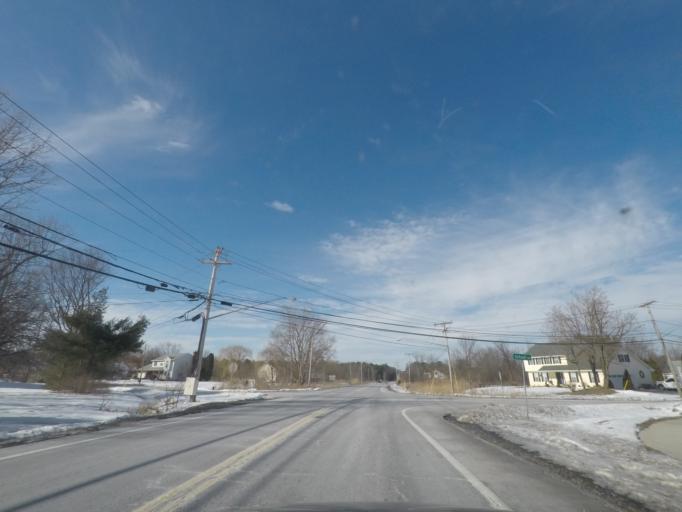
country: US
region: New York
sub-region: Albany County
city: Voorheesville
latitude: 42.6968
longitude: -73.9700
